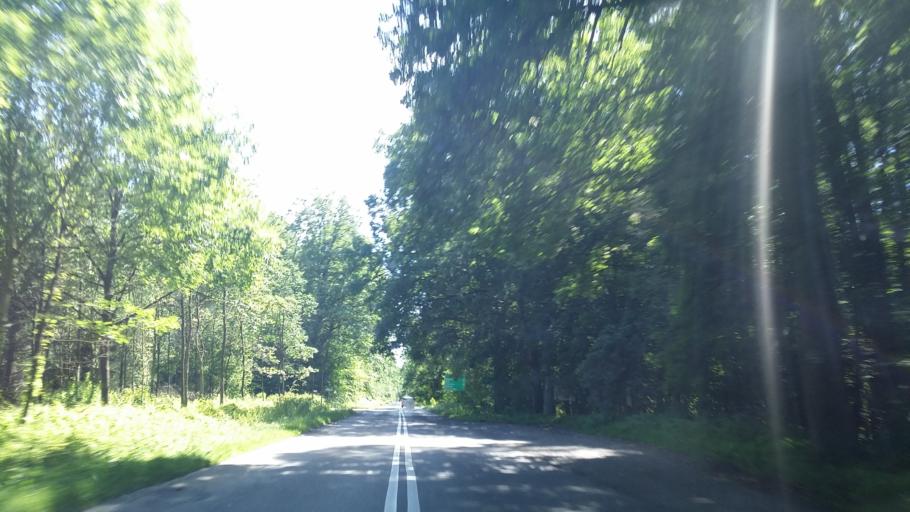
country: PL
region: West Pomeranian Voivodeship
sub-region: Powiat lobeski
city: Lobez
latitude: 53.6127
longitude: 15.6122
